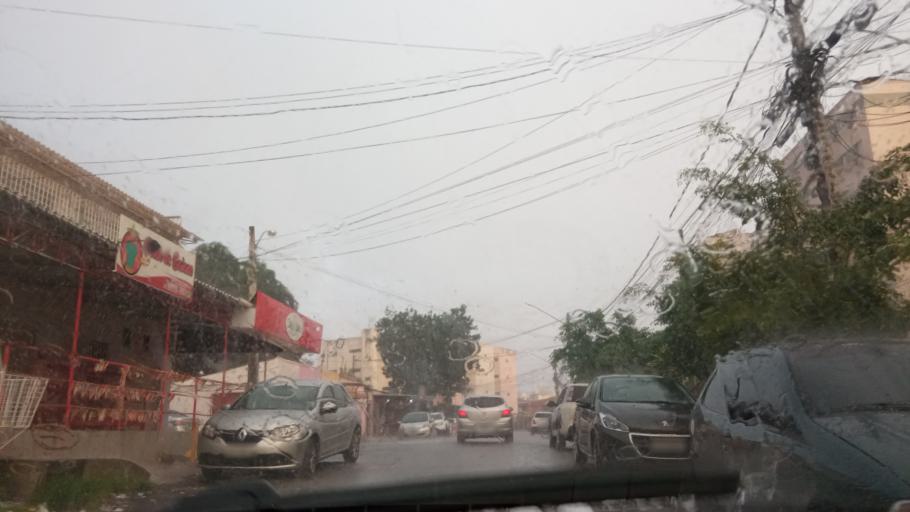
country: BR
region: Pernambuco
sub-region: Jaboatao Dos Guararapes
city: Jaboatao
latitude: -8.2017
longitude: -34.9248
